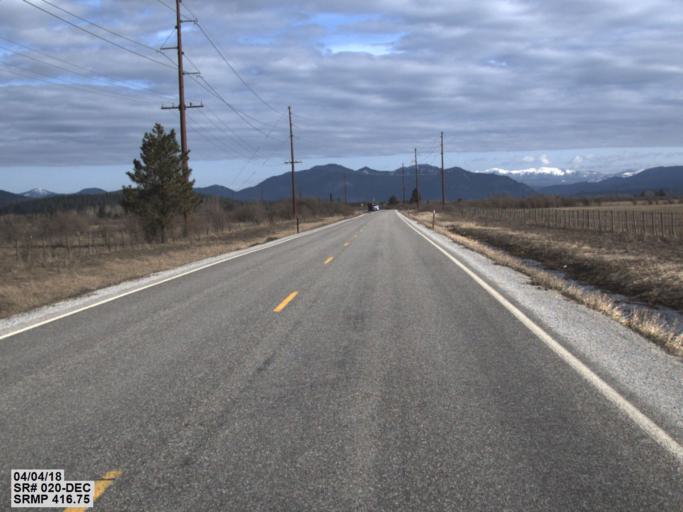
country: US
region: Washington
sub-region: Pend Oreille County
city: Newport
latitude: 48.3704
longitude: -117.3047
